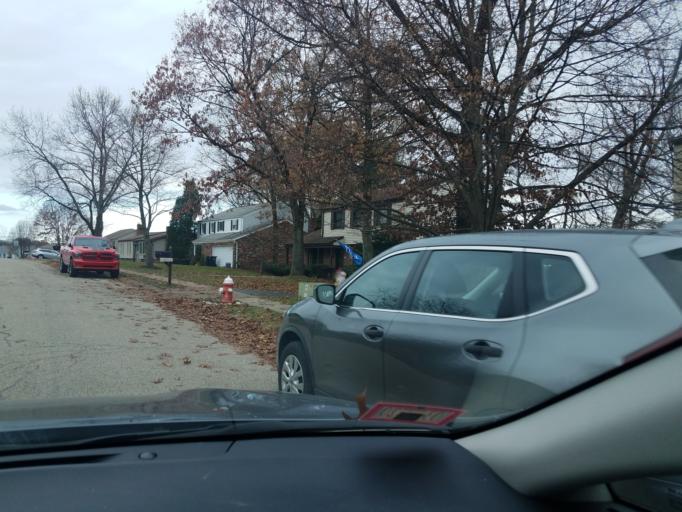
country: US
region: Pennsylvania
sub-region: Allegheny County
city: West View
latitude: 40.5541
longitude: -80.0595
